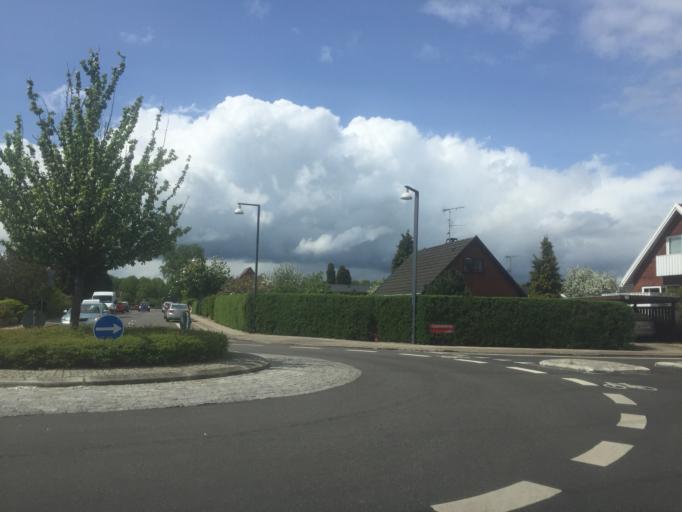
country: DK
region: Capital Region
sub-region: Rodovre Kommune
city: Rodovre
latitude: 55.6857
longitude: 12.4413
